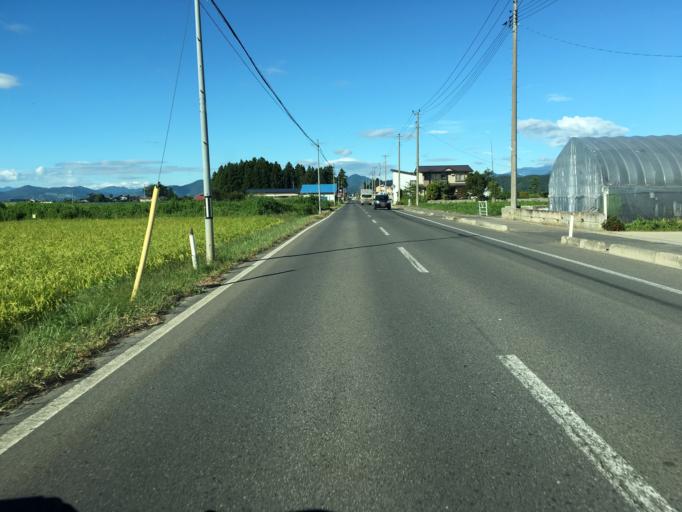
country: JP
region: Yamagata
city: Takahata
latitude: 37.9654
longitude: 140.1565
